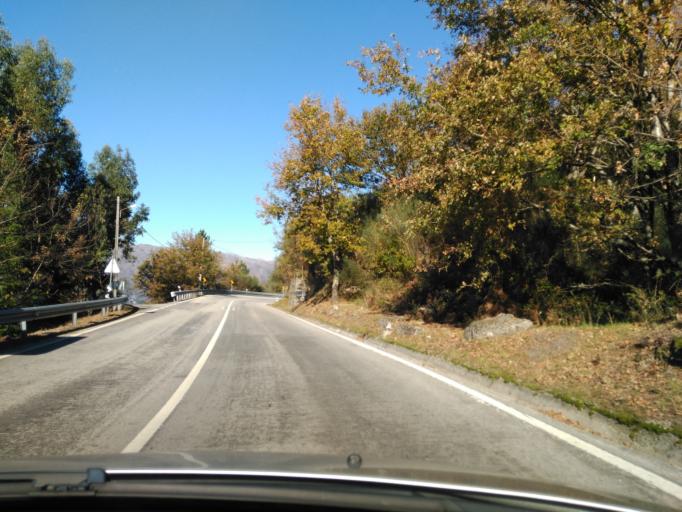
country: PT
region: Braga
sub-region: Vieira do Minho
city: Vieira do Minho
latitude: 41.6811
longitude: -8.0144
